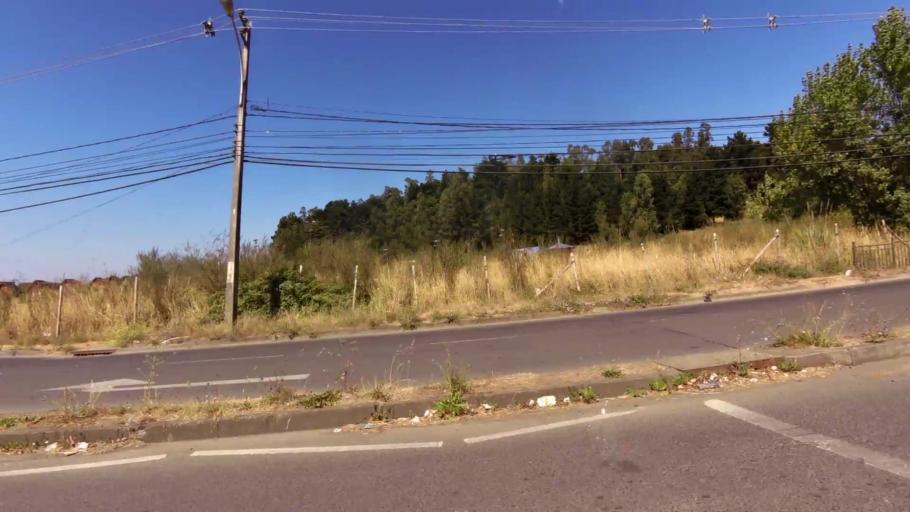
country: CL
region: Biobio
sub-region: Provincia de Concepcion
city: Concepcion
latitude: -36.7837
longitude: -73.0545
